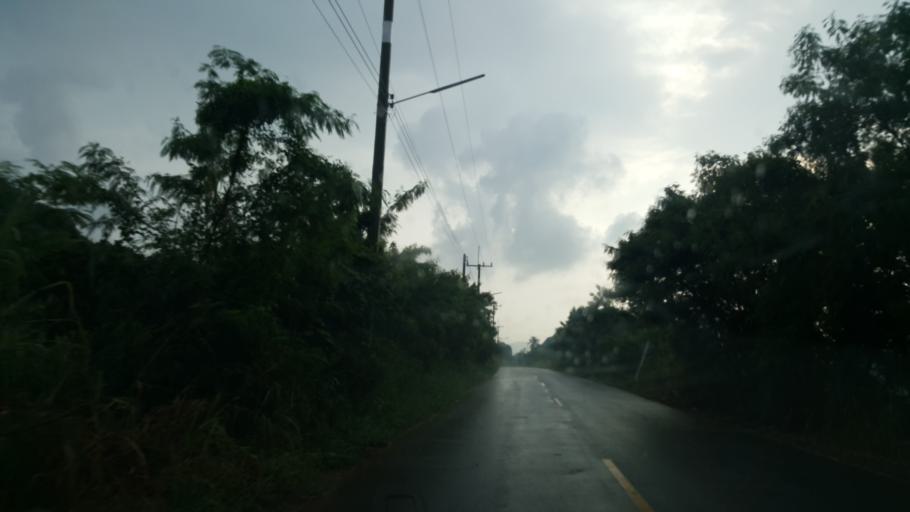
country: TH
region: Chon Buri
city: Sattahip
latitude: 12.7043
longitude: 100.9064
